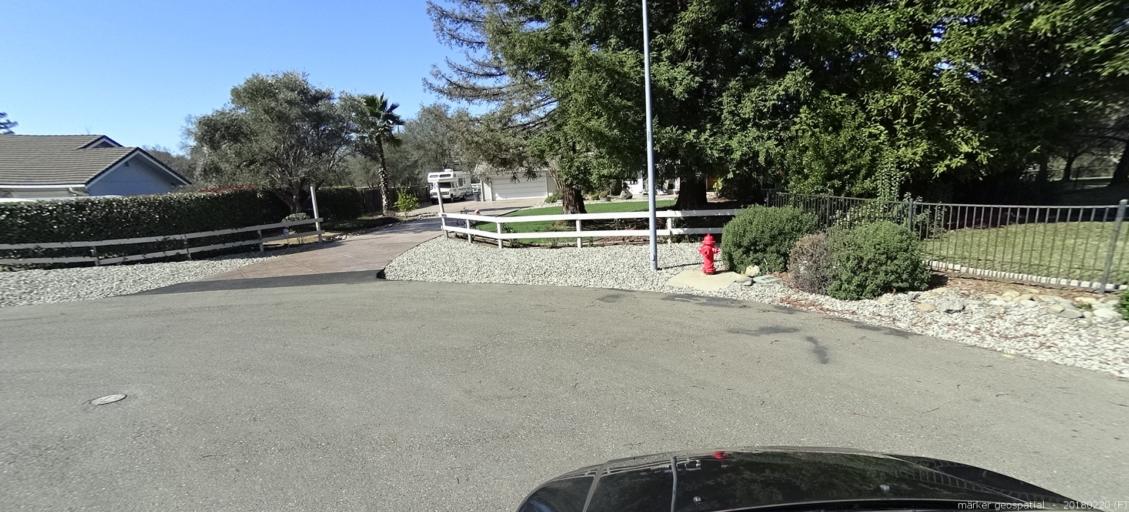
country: US
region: California
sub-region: Sacramento County
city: Orangevale
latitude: 38.6943
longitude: -121.2188
